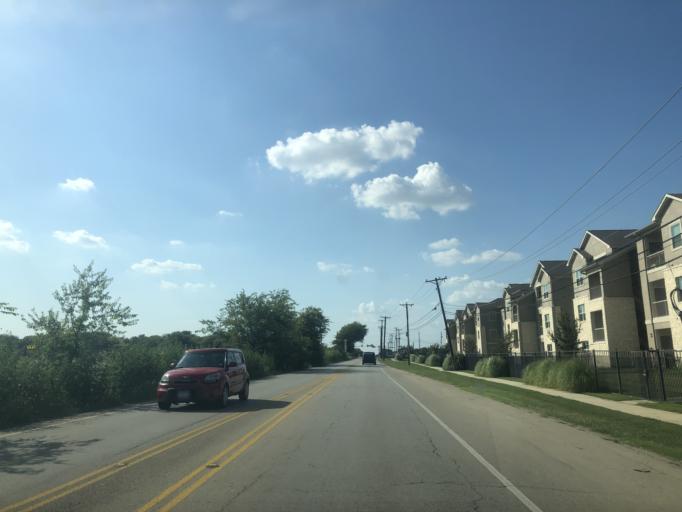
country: US
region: Texas
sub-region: Tarrant County
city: Saginaw
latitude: 32.8453
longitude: -97.3846
